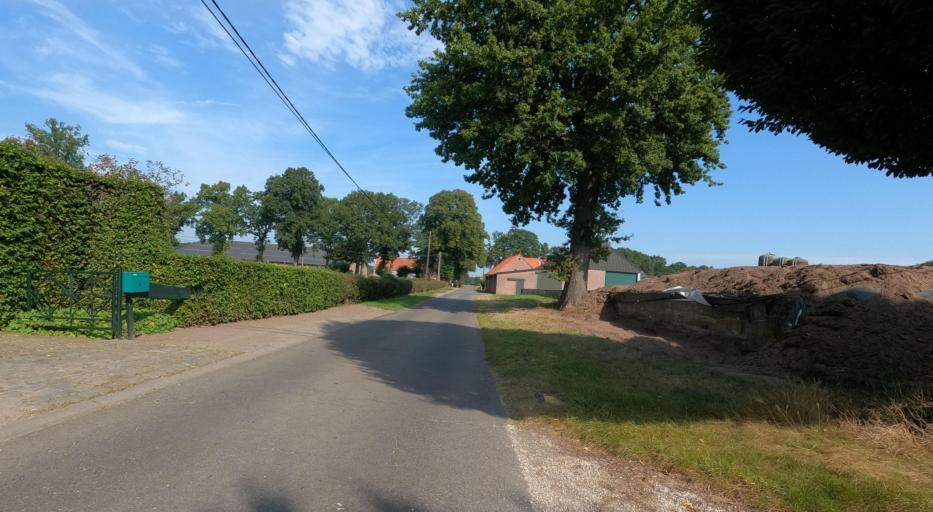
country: BE
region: Flanders
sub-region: Provincie Antwerpen
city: Essen
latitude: 51.4424
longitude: 4.4685
